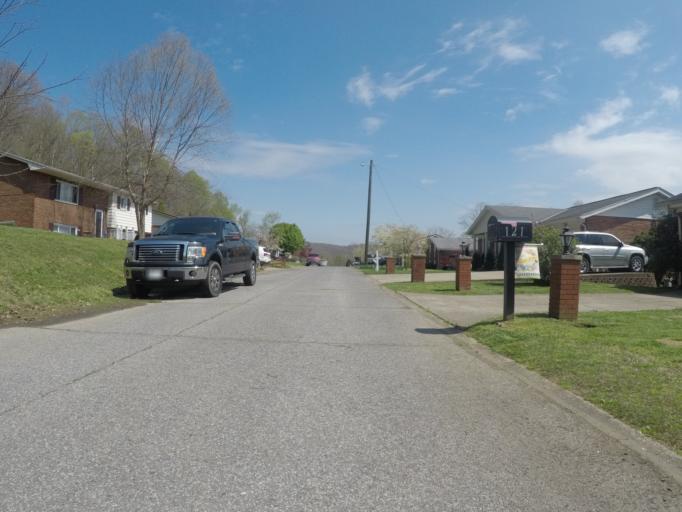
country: US
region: Ohio
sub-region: Lawrence County
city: Burlington
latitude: 38.3850
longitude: -82.5249
